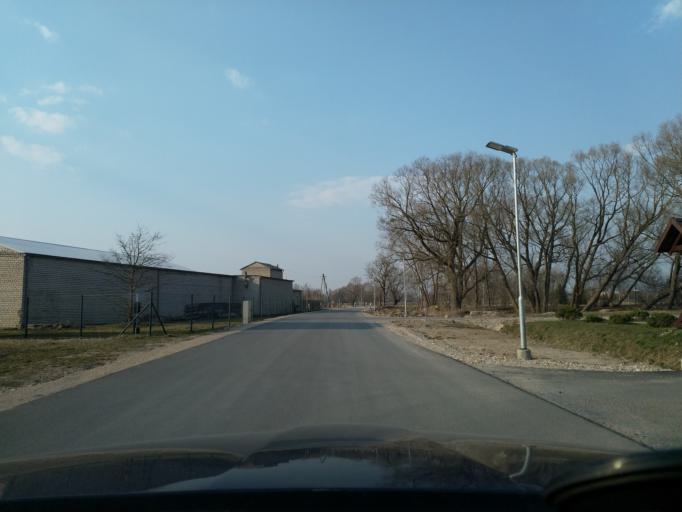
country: LV
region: Grobina
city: Grobina
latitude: 56.5344
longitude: 21.1824
